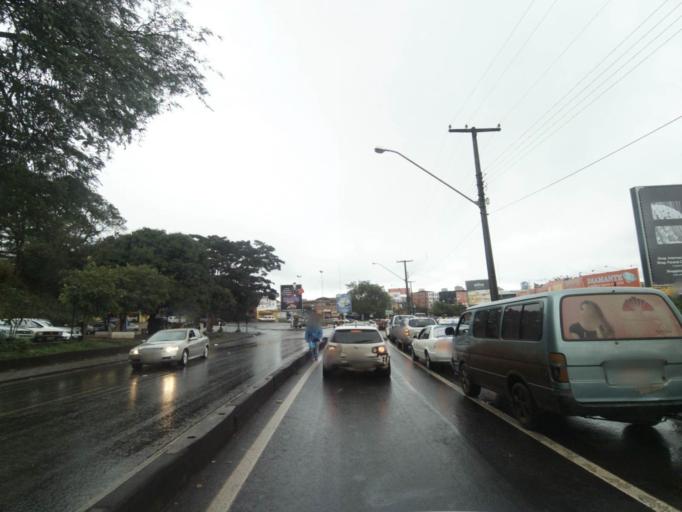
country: PY
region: Alto Parana
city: Ciudad del Este
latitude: -25.5088
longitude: -54.5929
